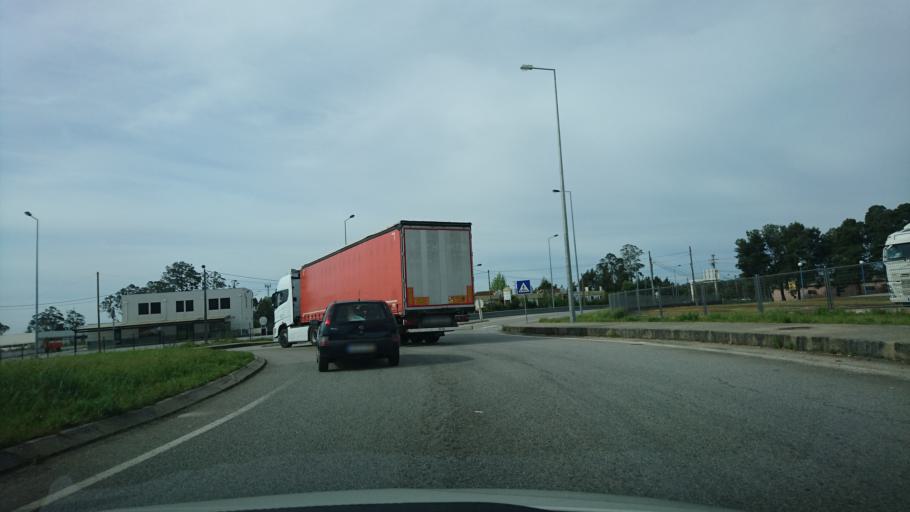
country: PT
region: Aveiro
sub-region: Albergaria-A-Velha
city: Albergaria-a-Velha
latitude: 40.7065
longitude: -8.4834
